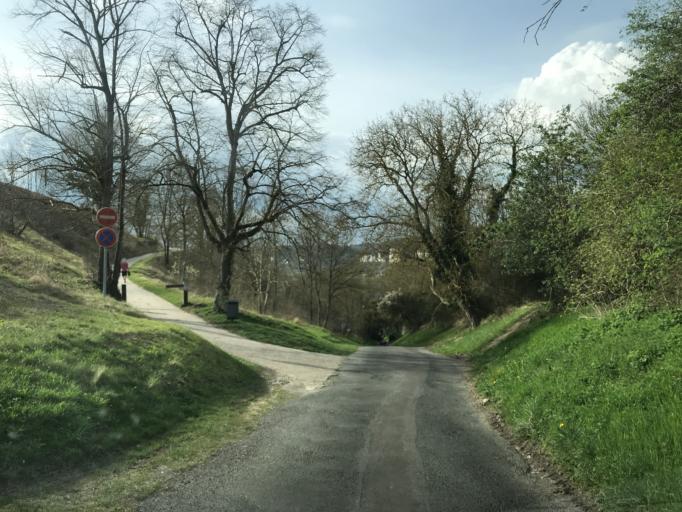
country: FR
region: Haute-Normandie
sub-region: Departement de l'Eure
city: Les Andelys
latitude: 49.2384
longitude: 1.4045
